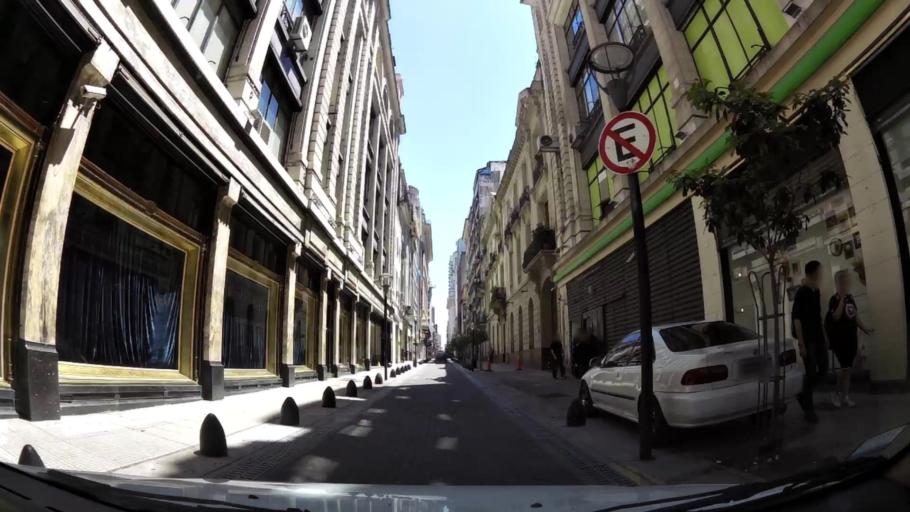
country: AR
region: Buenos Aires F.D.
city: Buenos Aires
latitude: -34.6058
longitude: -58.3757
